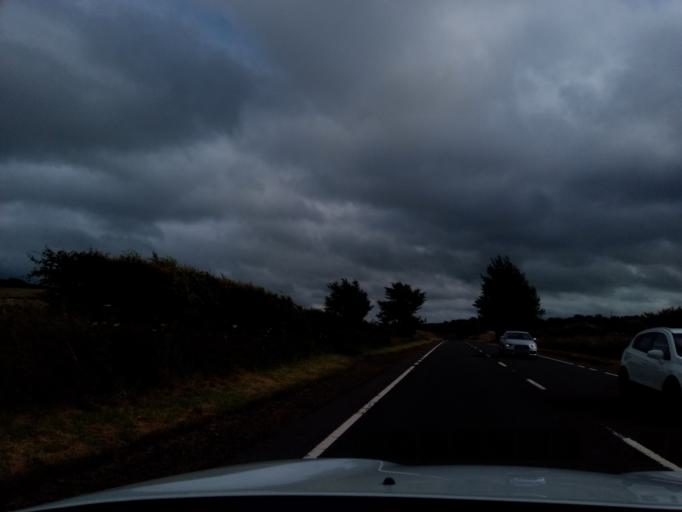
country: GB
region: Scotland
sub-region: The Scottish Borders
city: Lauder
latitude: 55.6948
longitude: -2.7114
